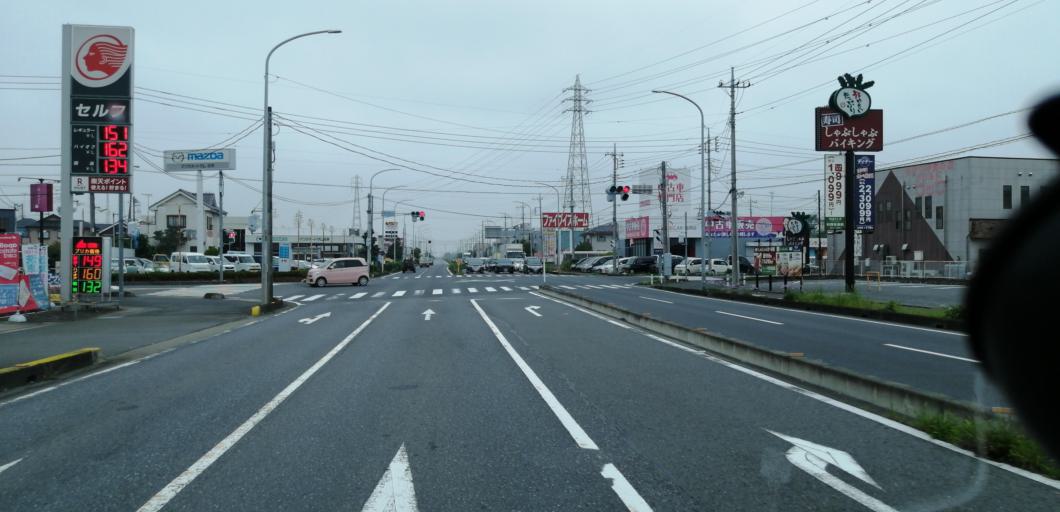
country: JP
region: Saitama
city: Kazo
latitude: 36.1331
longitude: 139.6023
